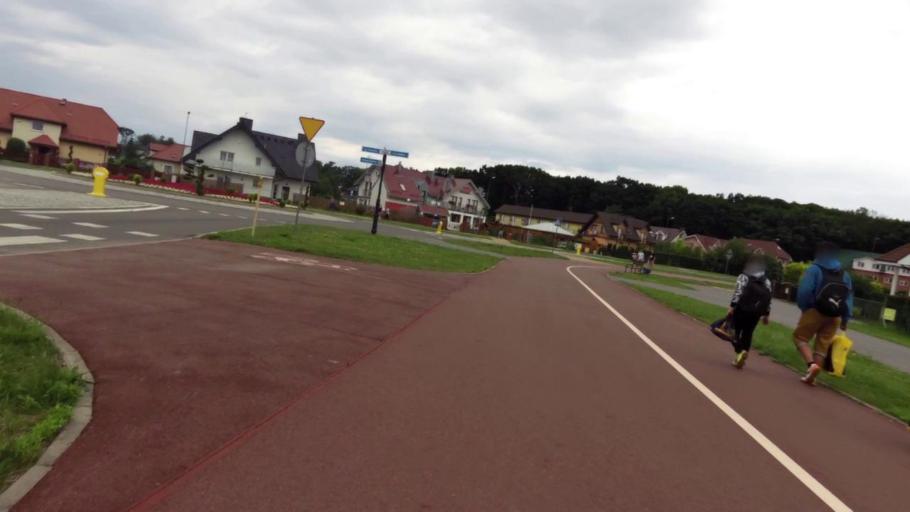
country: PL
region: West Pomeranian Voivodeship
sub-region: Powiat gryficki
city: Rewal
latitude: 54.0819
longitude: 15.0315
